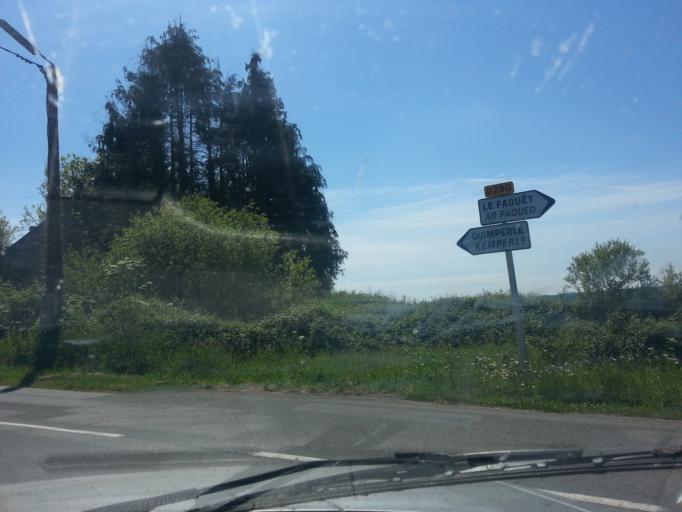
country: FR
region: Brittany
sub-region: Departement du Morbihan
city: Le Faouet
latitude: 48.0166
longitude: -3.4902
